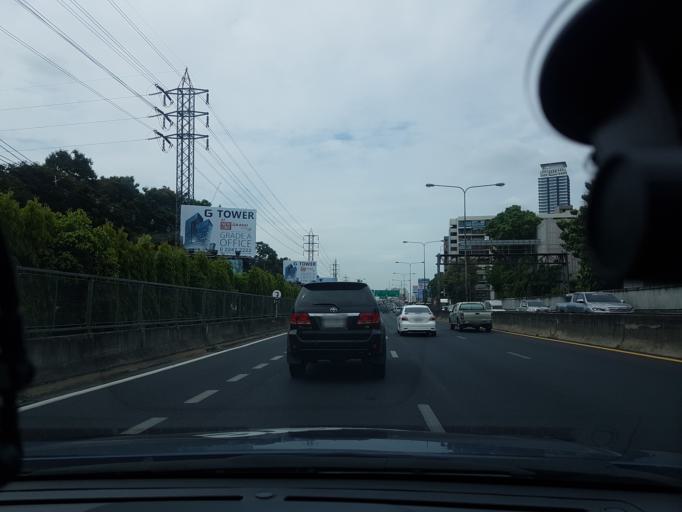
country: TH
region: Bangkok
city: Khlong Toei
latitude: 13.7277
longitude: 100.5521
